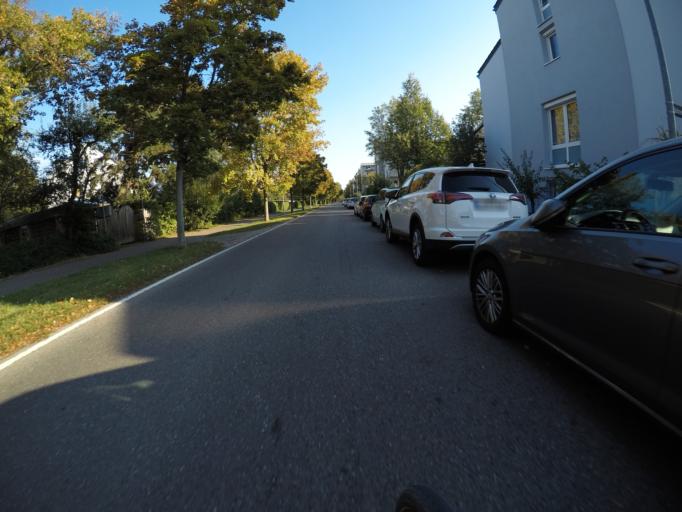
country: DE
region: Baden-Wuerttemberg
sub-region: Regierungsbezirk Stuttgart
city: Leinfelden-Echterdingen
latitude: 48.7157
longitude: 9.1975
